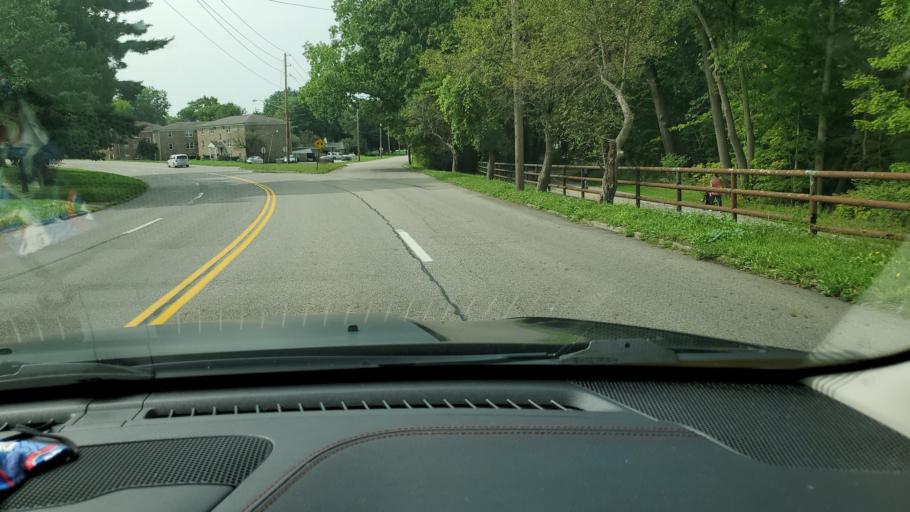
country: US
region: Ohio
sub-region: Mahoning County
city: Boardman
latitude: 41.0501
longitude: -80.6734
